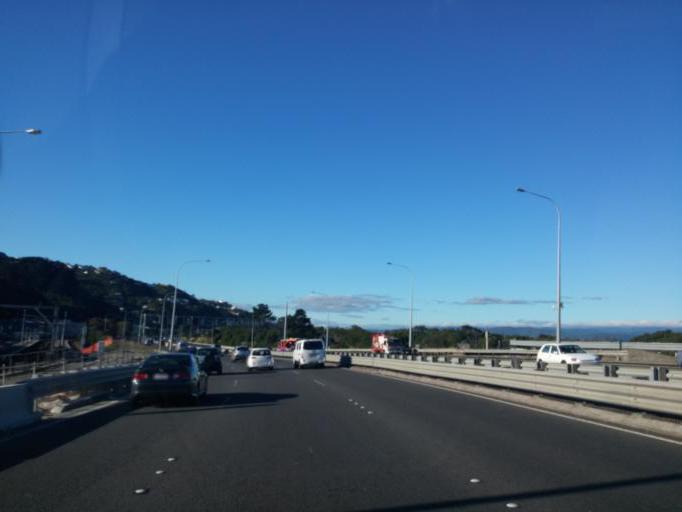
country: NZ
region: Wellington
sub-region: Wellington City
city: Wellington
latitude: -41.2614
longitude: 174.7900
